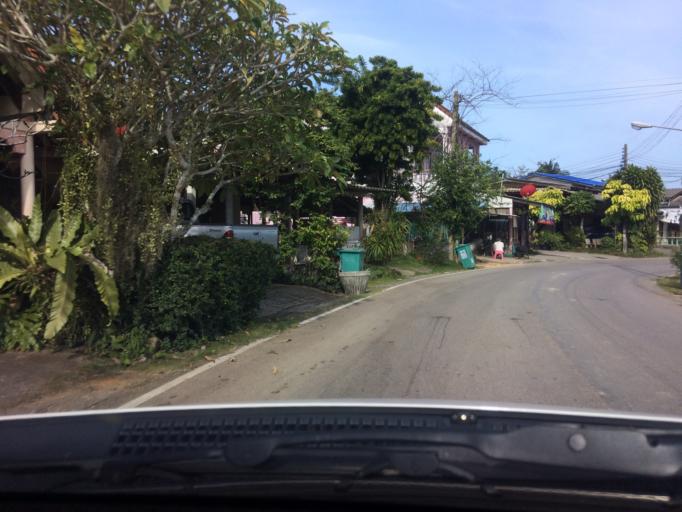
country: TH
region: Phuket
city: Thalang
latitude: 8.0438
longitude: 98.3296
